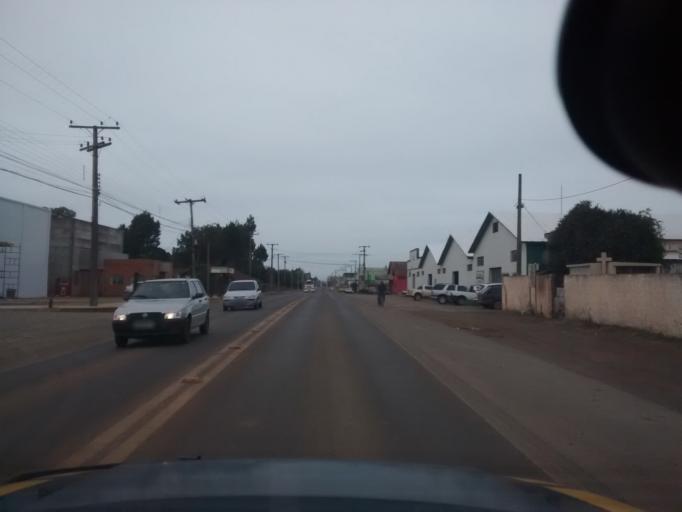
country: BR
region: Rio Grande do Sul
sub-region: Vacaria
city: Vacaria
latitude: -28.4923
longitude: -50.9554
